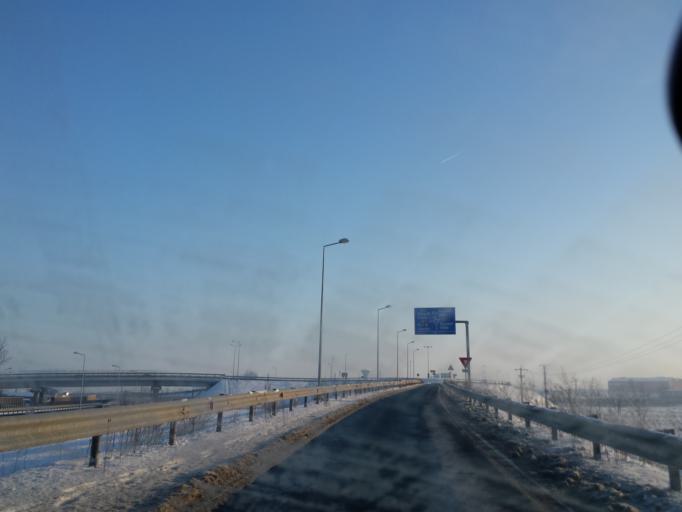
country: RO
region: Alba
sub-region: Municipiul Sebes
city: Lancram
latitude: 45.9760
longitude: 23.5549
